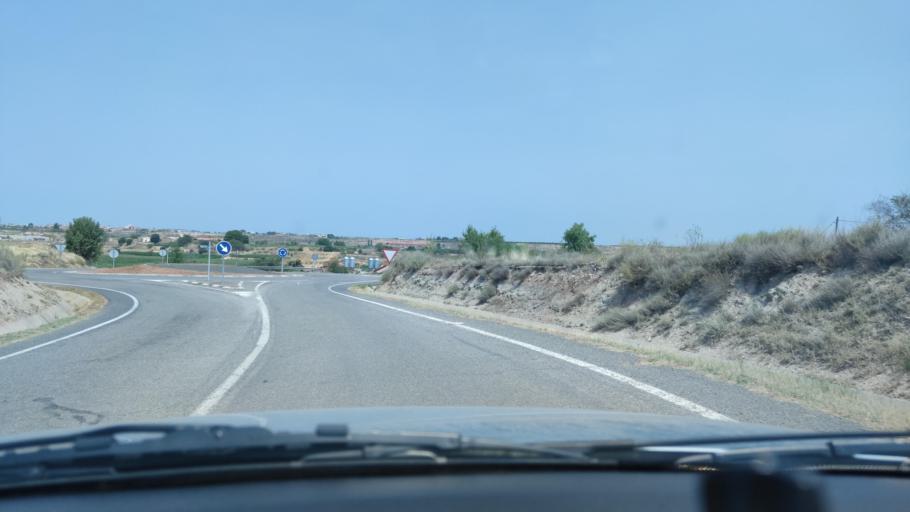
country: ES
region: Catalonia
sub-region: Provincia de Lleida
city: Bellpuig
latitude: 41.6110
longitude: 1.0309
